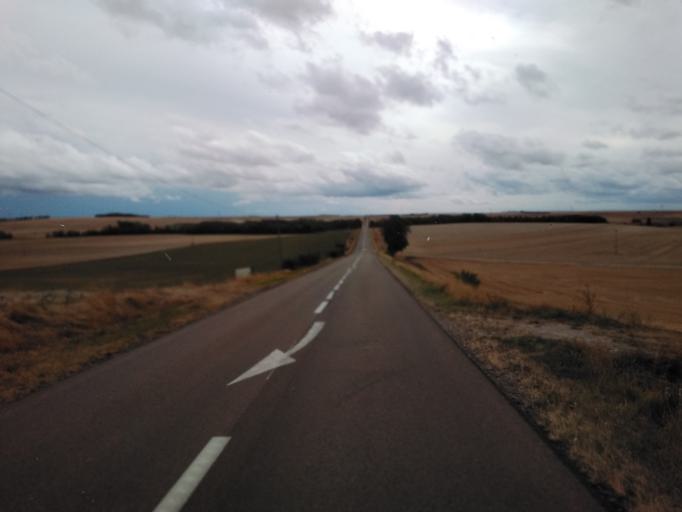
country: FR
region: Champagne-Ardenne
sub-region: Departement de l'Aube
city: Brienne-le-Chateau
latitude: 48.5507
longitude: 4.5223
